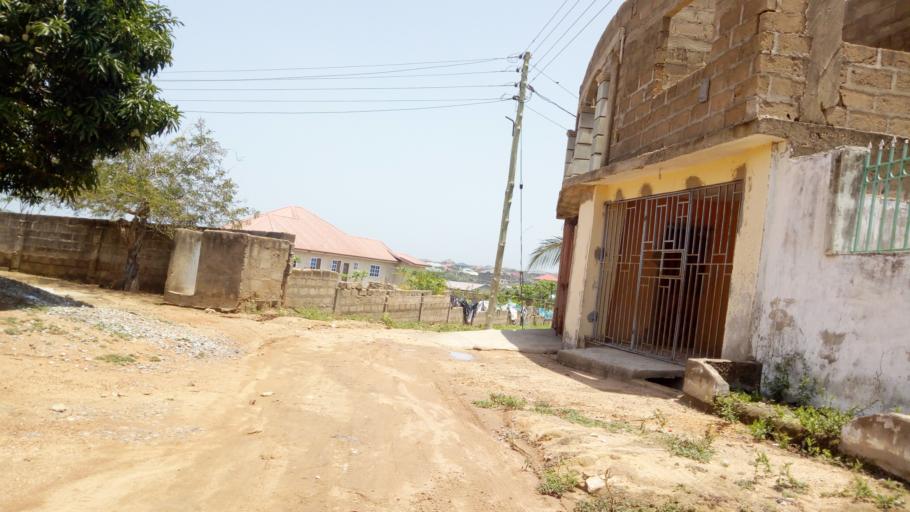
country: GH
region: Central
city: Kasoa
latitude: 5.5030
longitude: -0.4530
